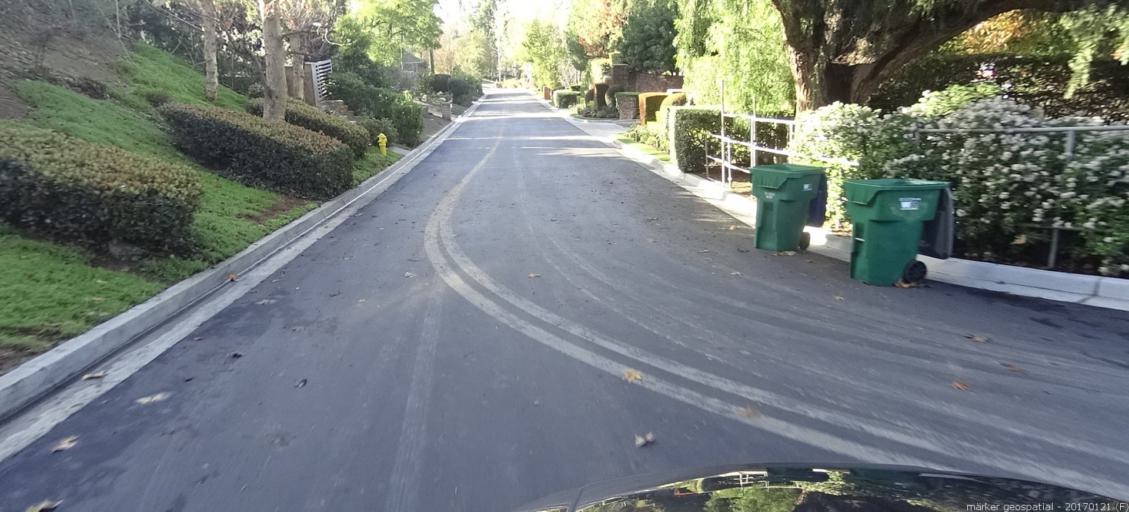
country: US
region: California
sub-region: Orange County
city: North Tustin
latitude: 33.7573
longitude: -117.7813
